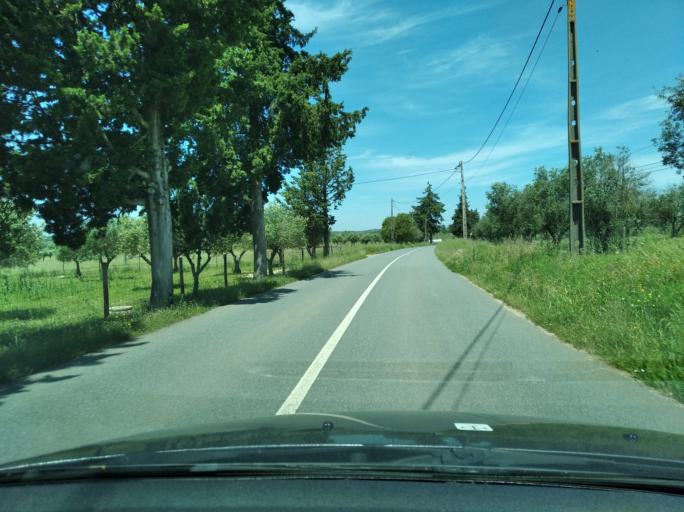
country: PT
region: Portalegre
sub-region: Avis
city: Avis
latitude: 39.0892
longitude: -7.8801
